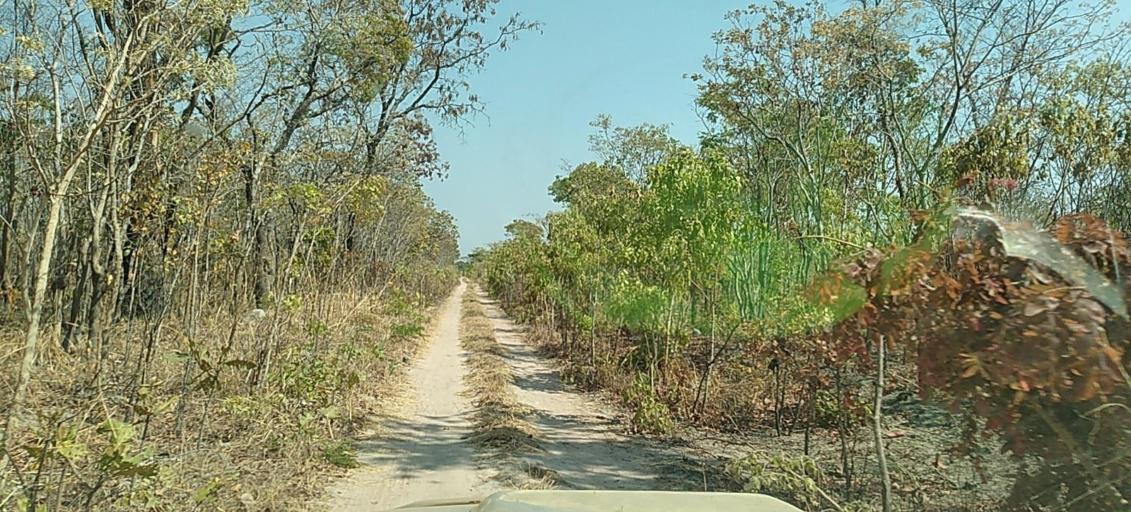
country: ZM
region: North-Western
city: Kalengwa
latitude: -13.3204
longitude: 24.8215
